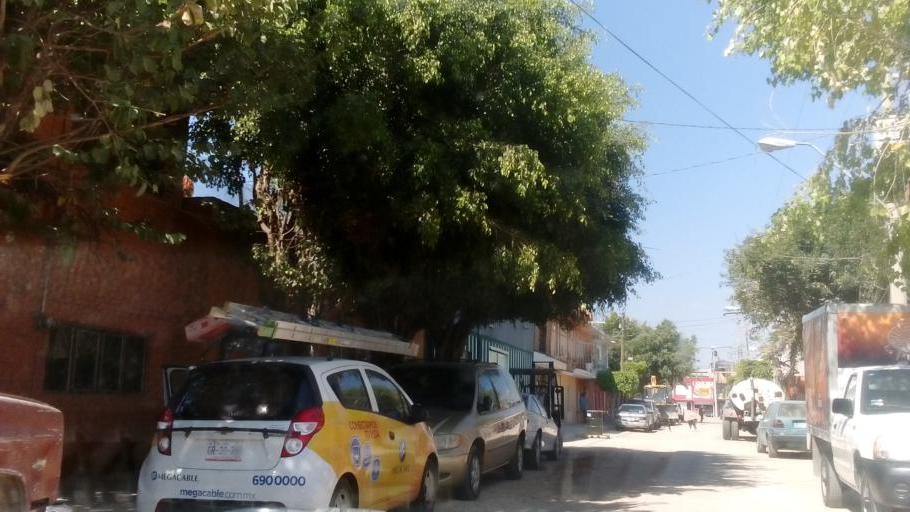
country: MX
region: Guanajuato
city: Leon
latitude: 21.1499
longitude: -101.6856
